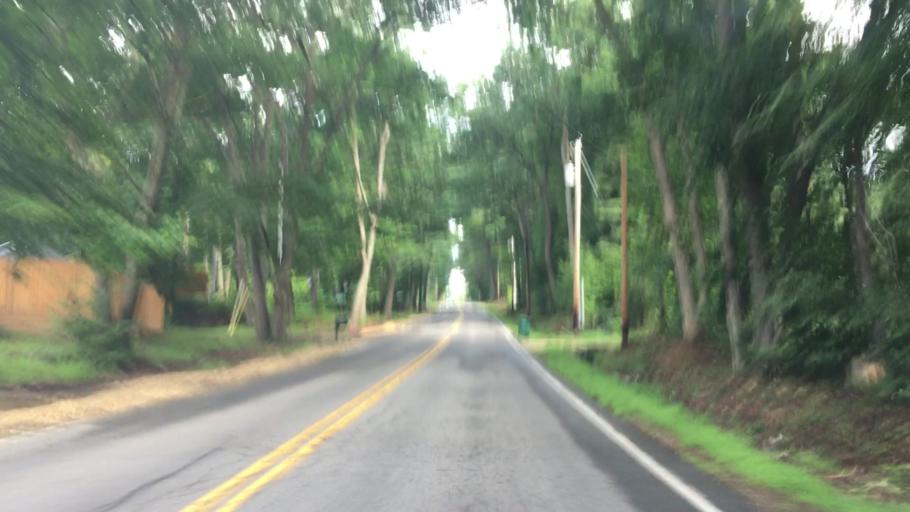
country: US
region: New Hampshire
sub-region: Strafford County
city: Rochester
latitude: 43.3575
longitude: -70.9917
